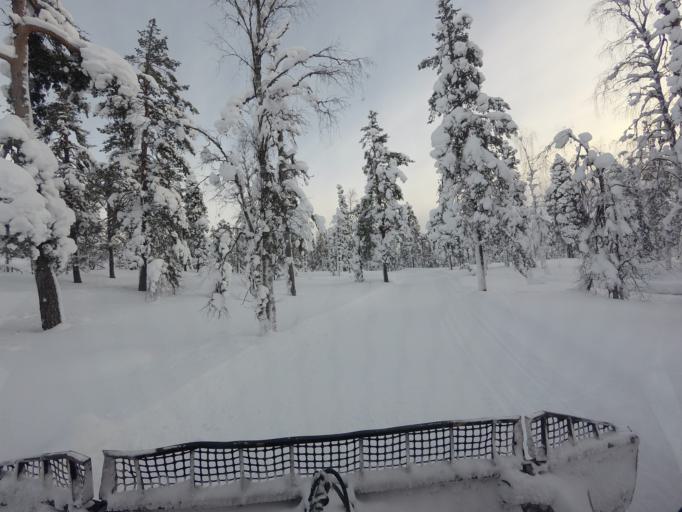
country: FI
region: Lapland
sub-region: Tunturi-Lappi
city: Kolari
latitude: 67.6511
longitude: 24.2420
